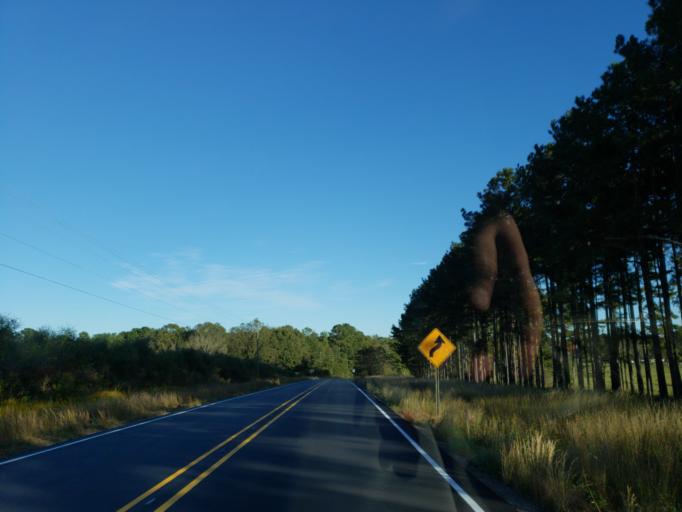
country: US
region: Mississippi
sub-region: Perry County
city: Richton
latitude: 31.3568
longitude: -88.7902
